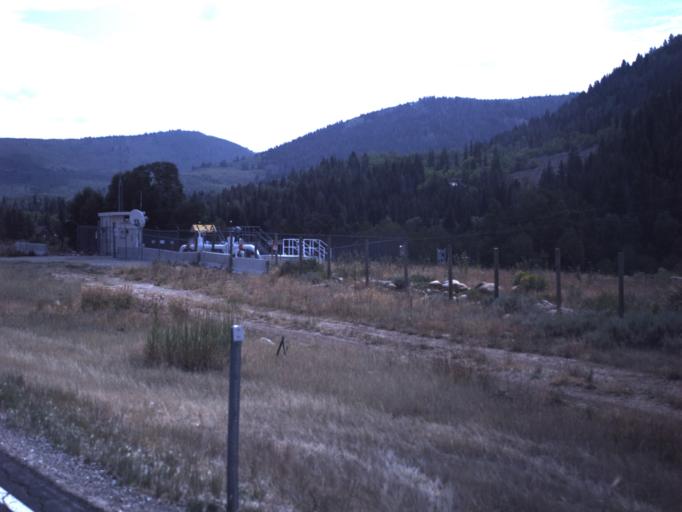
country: US
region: Utah
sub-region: Summit County
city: Francis
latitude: 40.5515
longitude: -111.1560
